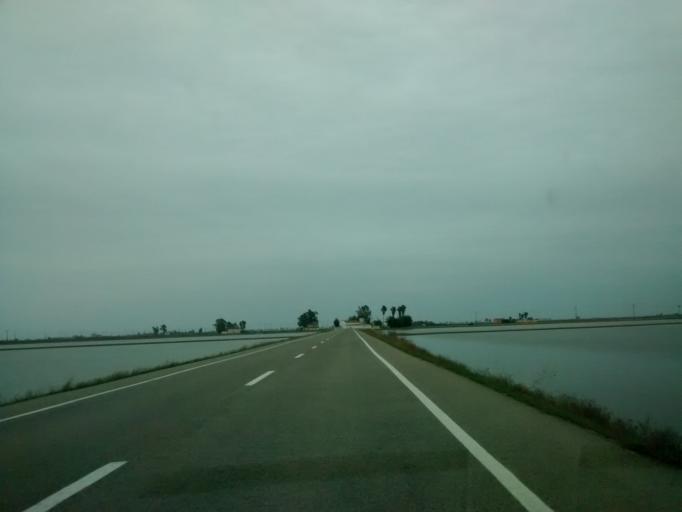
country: ES
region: Catalonia
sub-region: Provincia de Tarragona
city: Deltebre
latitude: 40.6871
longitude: 0.6892
